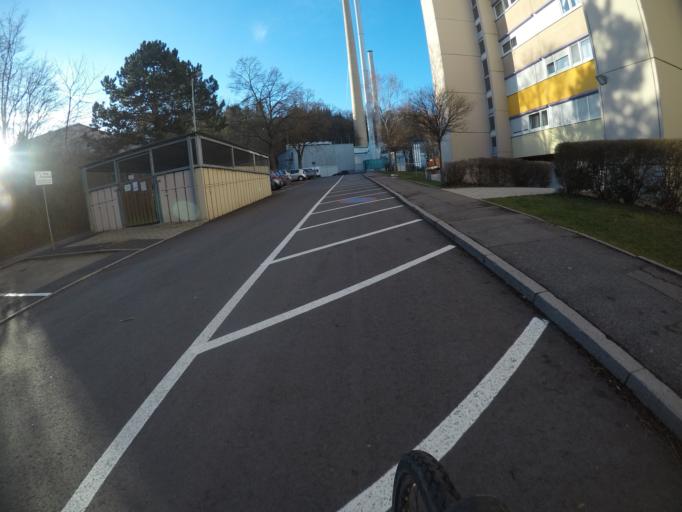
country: DE
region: Baden-Wuerttemberg
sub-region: Regierungsbezirk Stuttgart
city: Boeblingen
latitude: 48.6750
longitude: 9.0051
